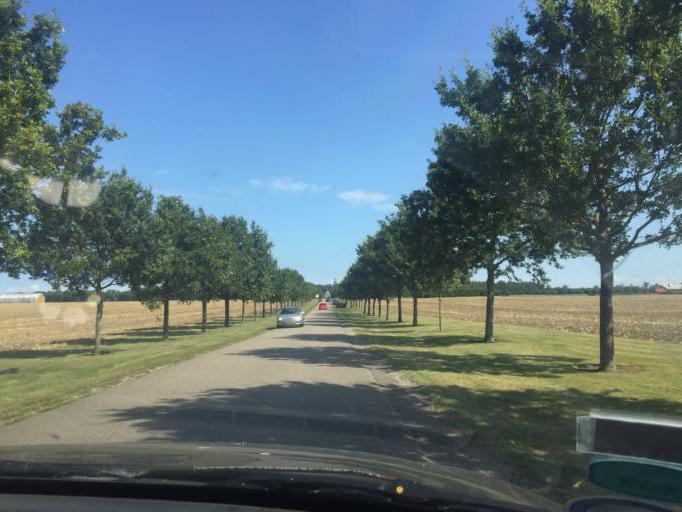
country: DK
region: Zealand
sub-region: Lolland Kommune
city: Maribo
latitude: 54.8029
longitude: 11.5079
